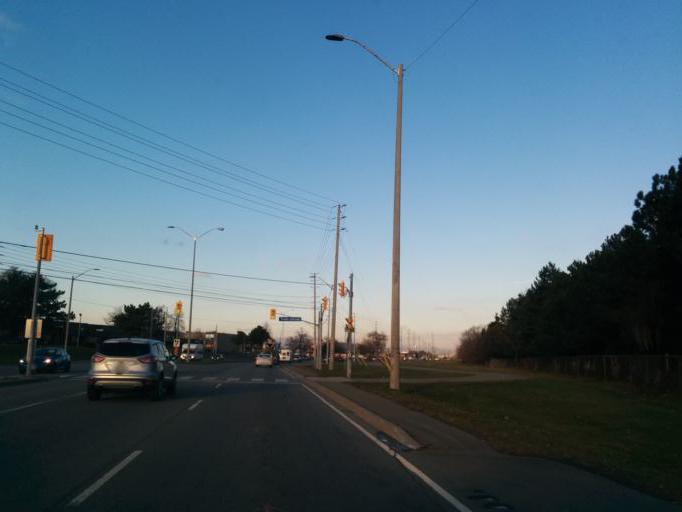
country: CA
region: Ontario
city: Mississauga
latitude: 43.5856
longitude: -79.5947
